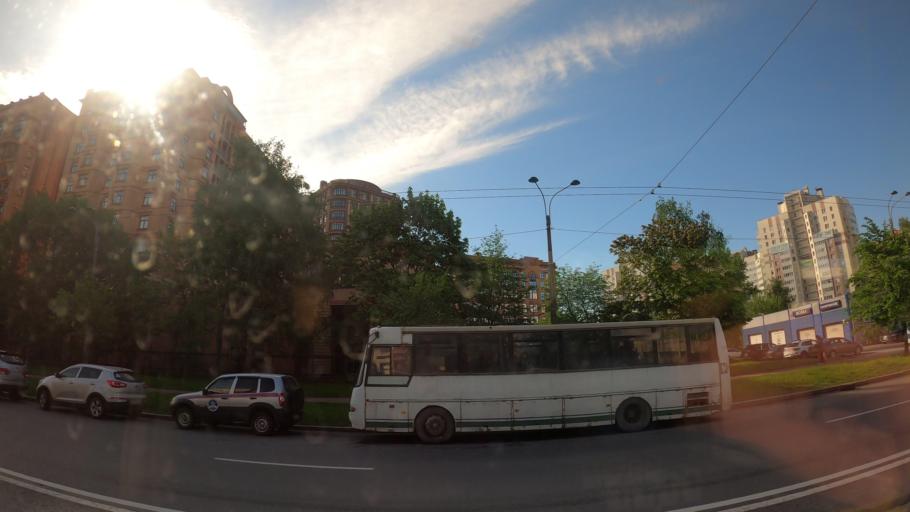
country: RU
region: St.-Petersburg
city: Vasyl'evsky Ostrov
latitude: 59.9417
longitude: 30.2262
